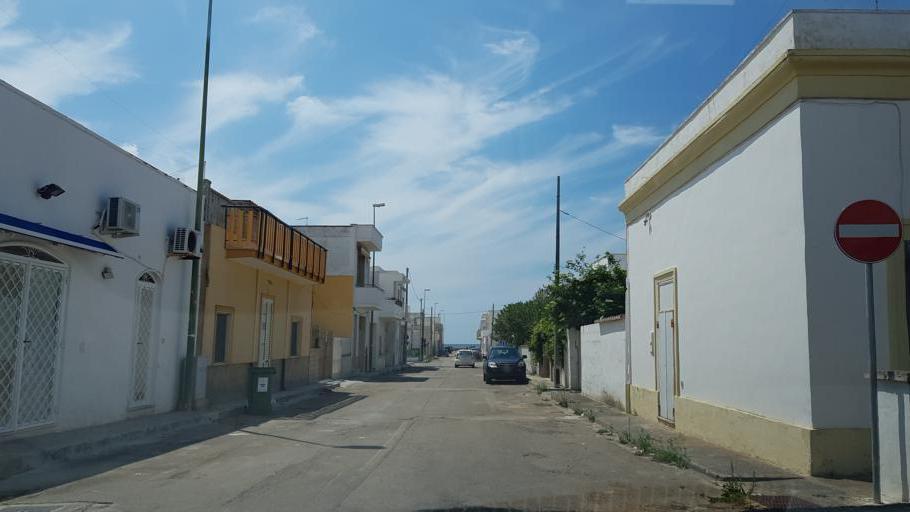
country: IT
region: Apulia
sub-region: Provincia di Lecce
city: Porto Cesareo
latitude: 40.2879
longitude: 17.8489
